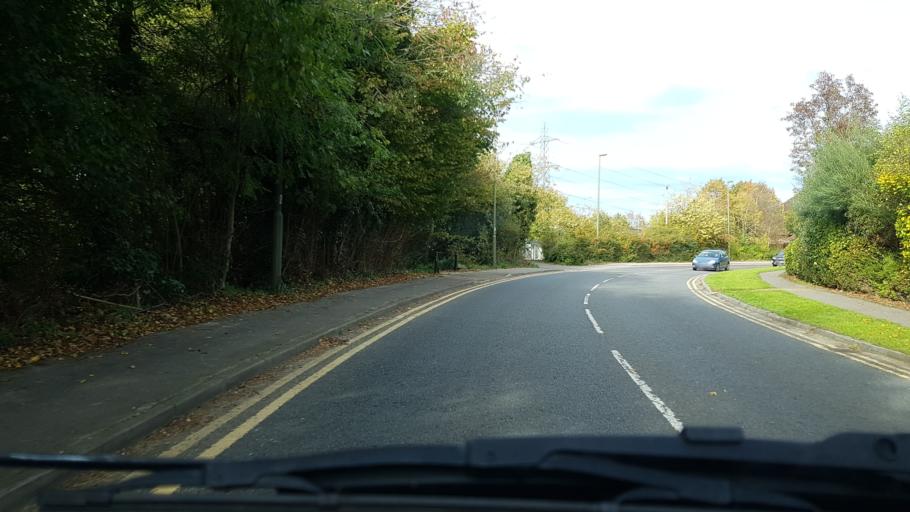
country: GB
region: England
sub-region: Surrey
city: Cobham
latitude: 51.3348
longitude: -0.4229
